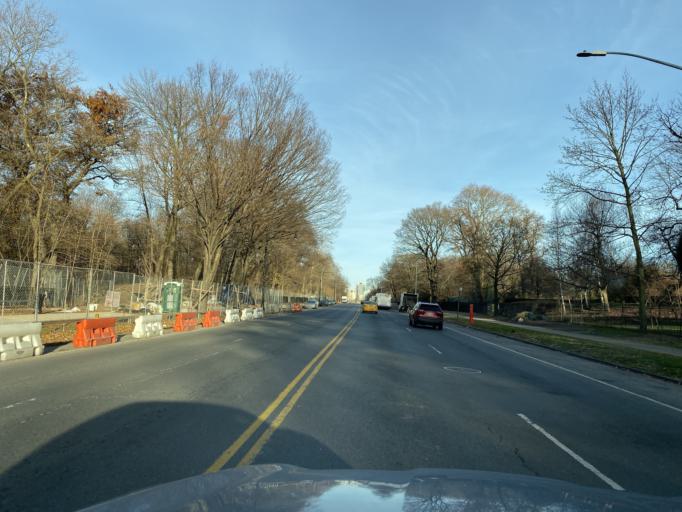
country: US
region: New York
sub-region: Kings County
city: Brooklyn
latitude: 40.6671
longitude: -73.9651
